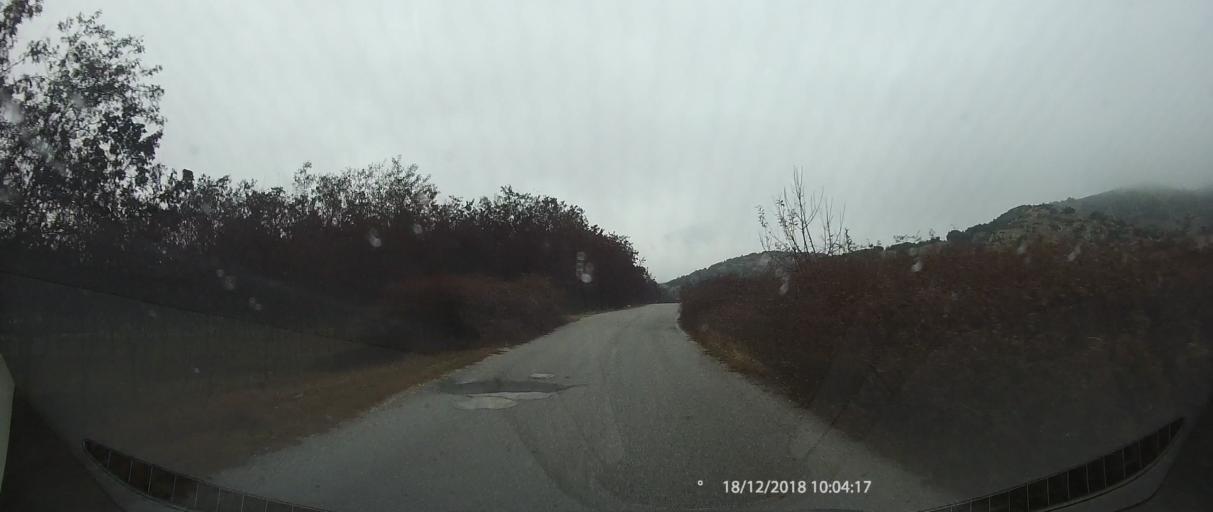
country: GR
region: Thessaly
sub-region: Nomos Larisis
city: Livadi
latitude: 40.0512
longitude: 22.2226
